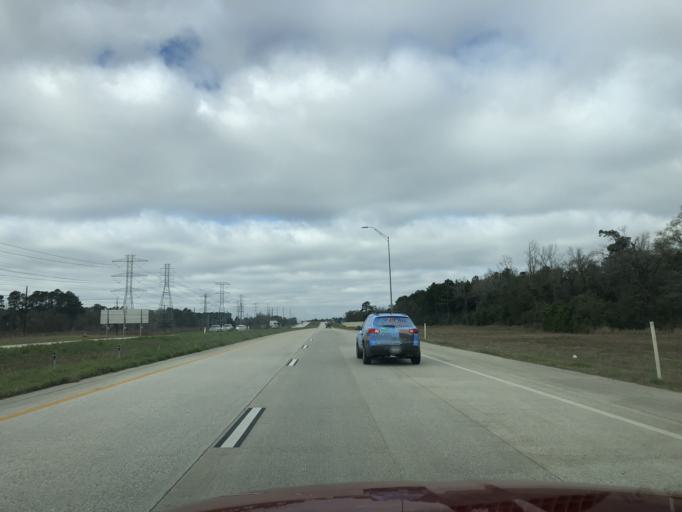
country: US
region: Texas
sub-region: Harris County
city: Spring
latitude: 30.0914
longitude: -95.4695
